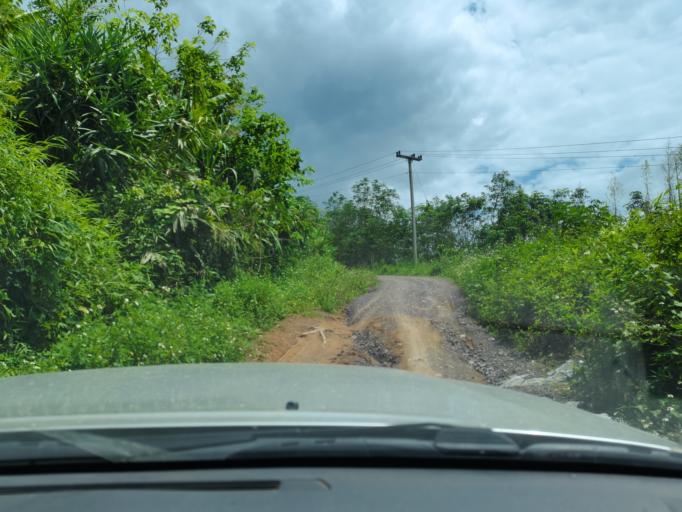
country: LA
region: Loungnamtha
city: Muang Long
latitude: 20.7196
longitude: 101.0137
